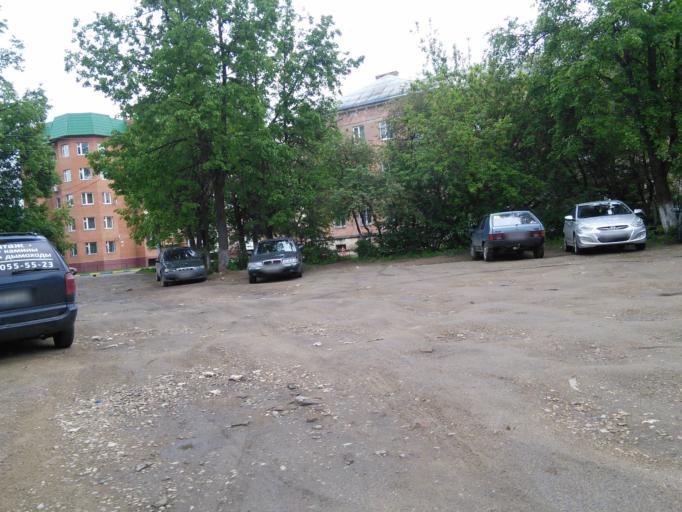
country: RU
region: Moskovskaya
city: Serpukhov
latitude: 54.9206
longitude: 37.3795
